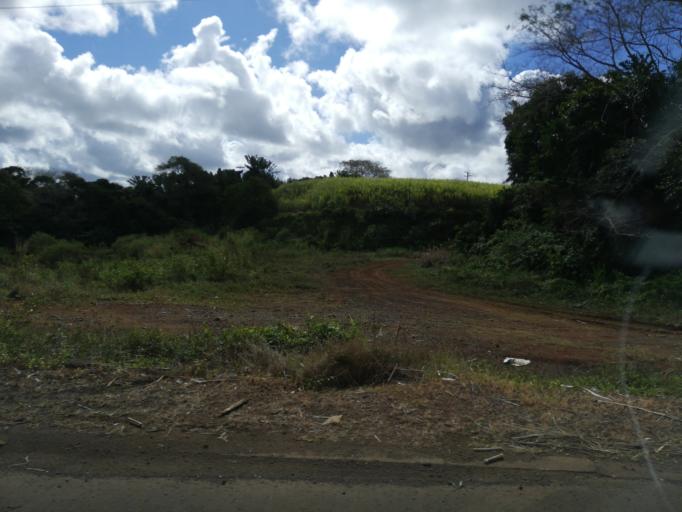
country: MU
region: Grand Port
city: Plaine Magnien
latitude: -20.4165
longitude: 57.6718
